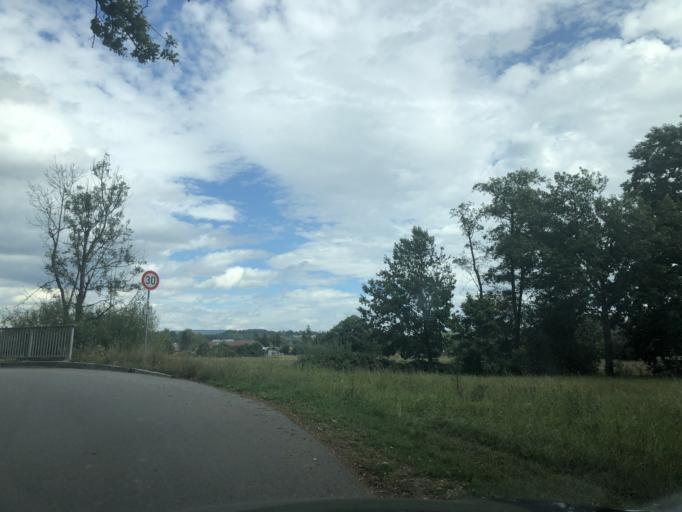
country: DE
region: Bavaria
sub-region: Upper Palatinate
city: Pressath
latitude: 49.7548
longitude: 11.9397
